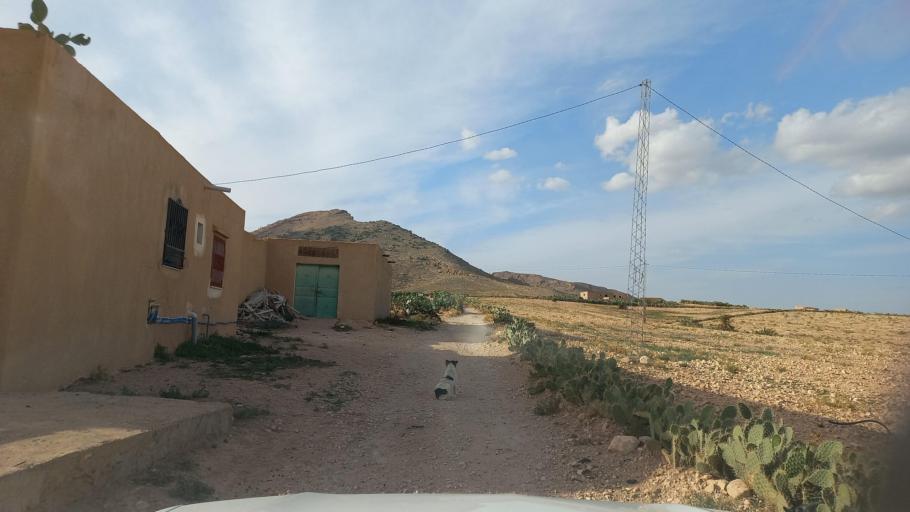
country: TN
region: Al Qasrayn
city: Sbiba
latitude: 35.4561
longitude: 9.0782
